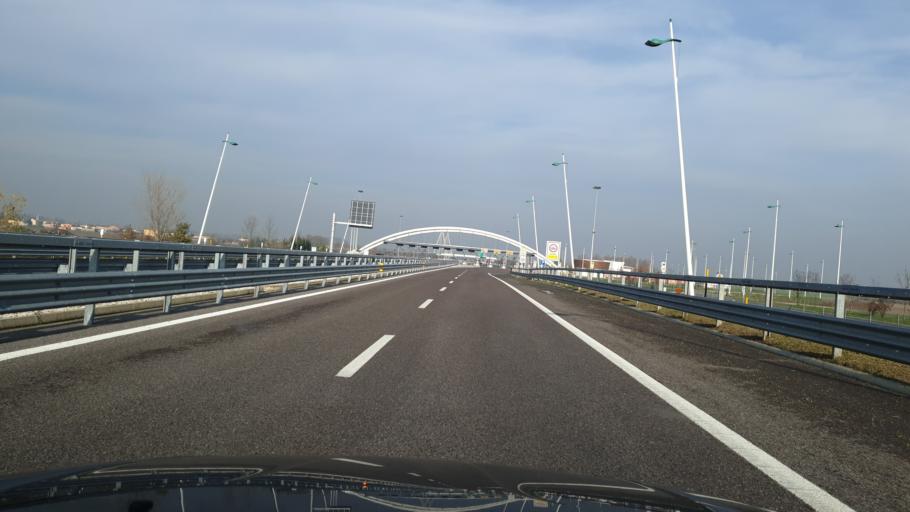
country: IT
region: Veneto
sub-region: Provincia di Padova
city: Piacenza d'Adige
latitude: 45.0985
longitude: 11.5293
